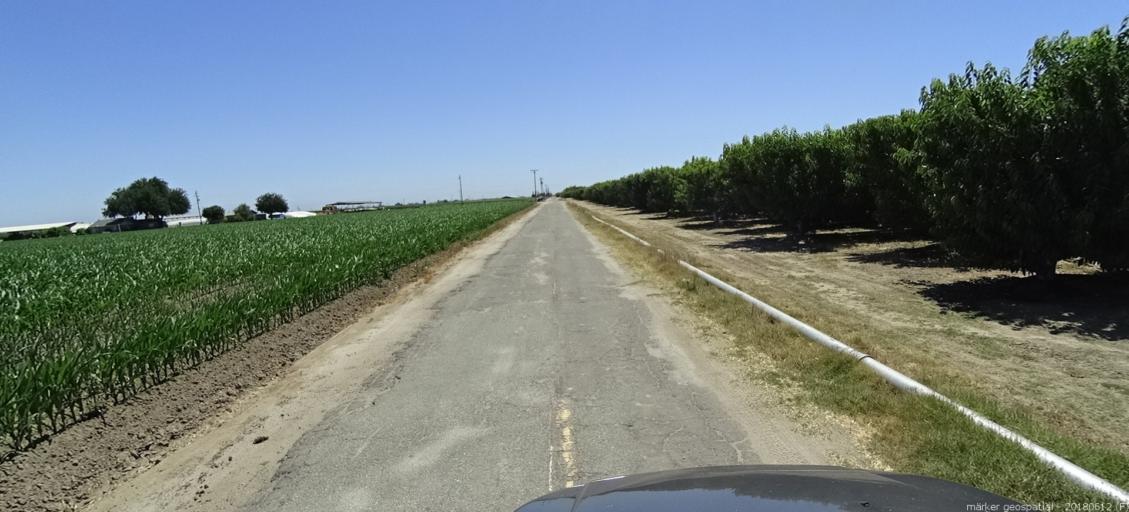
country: US
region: California
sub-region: Madera County
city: Chowchilla
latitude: 37.0616
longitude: -120.3643
